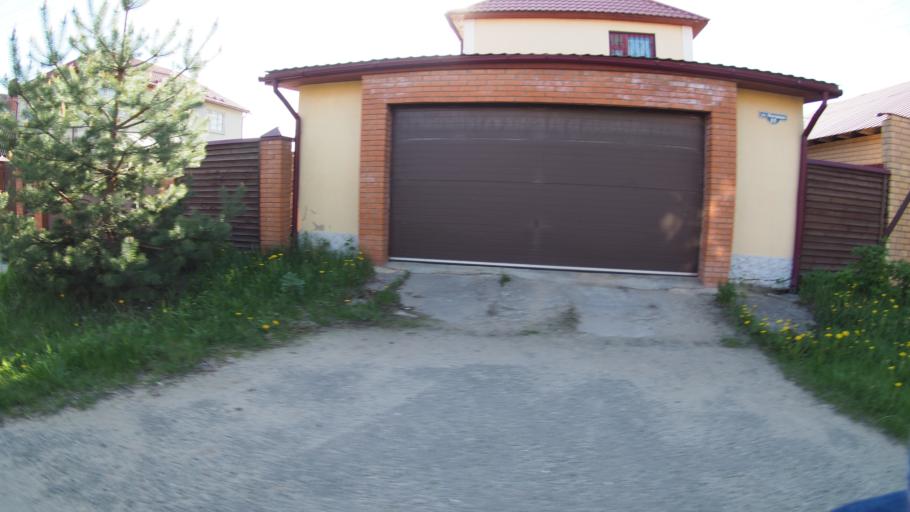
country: RU
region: Moskovskaya
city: Ramenskoye
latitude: 55.5492
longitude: 38.1934
